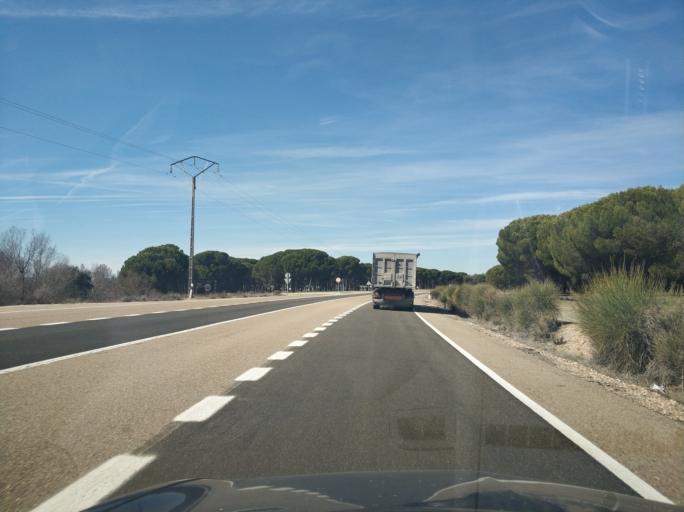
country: ES
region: Castille and Leon
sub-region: Provincia de Valladolid
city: Simancas
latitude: 41.5657
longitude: -4.7992
